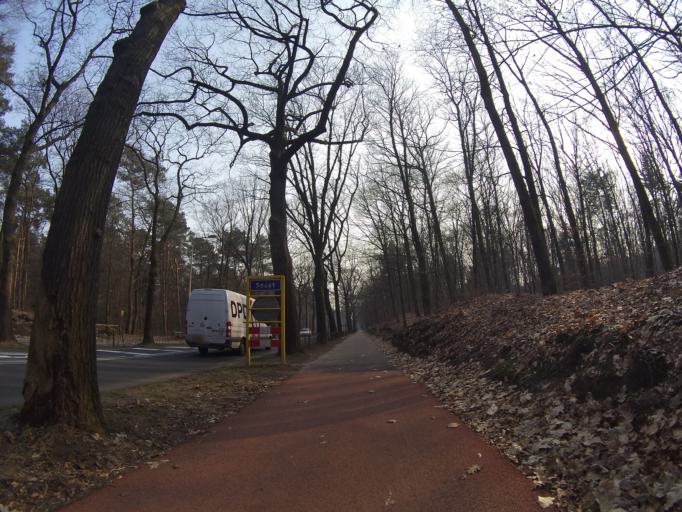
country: NL
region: Utrecht
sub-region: Gemeente Soest
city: Soest
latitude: 52.1561
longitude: 5.3058
